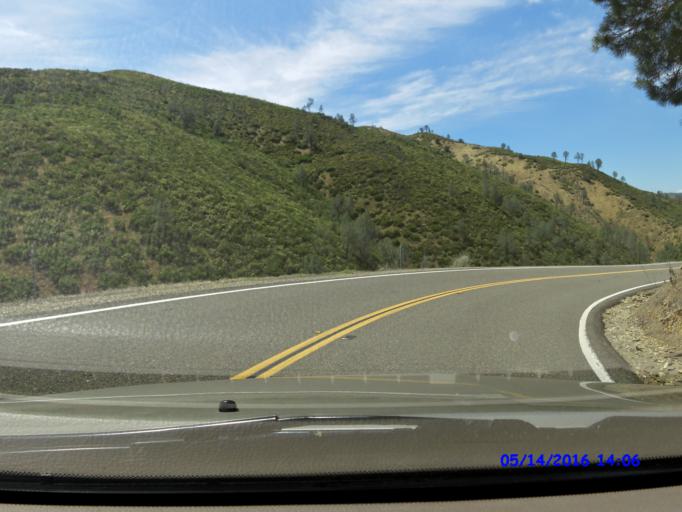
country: US
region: California
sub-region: Mariposa County
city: Mariposa
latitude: 37.5970
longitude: -120.1312
